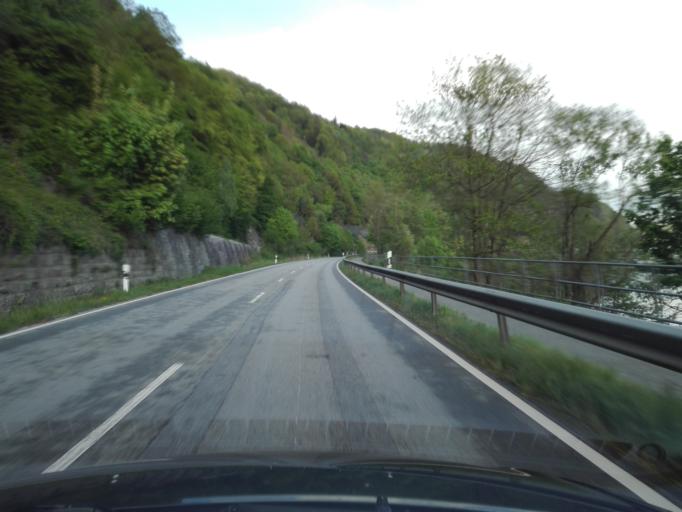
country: DE
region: Bavaria
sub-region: Lower Bavaria
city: Obernzell
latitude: 48.5707
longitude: 13.5935
